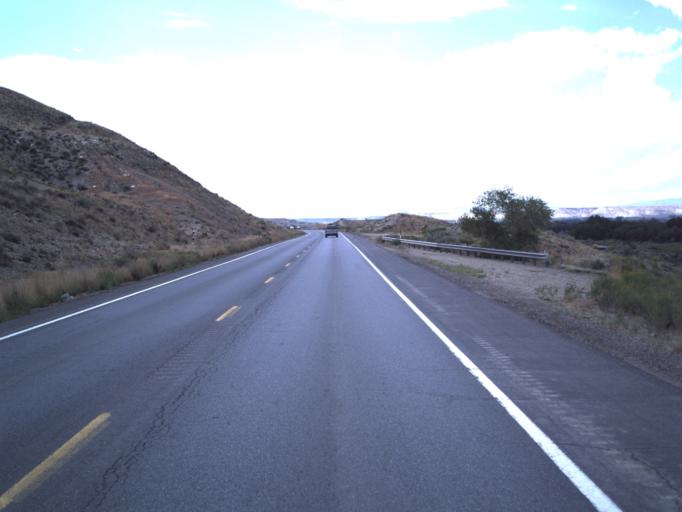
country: US
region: Utah
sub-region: Duchesne County
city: Duchesne
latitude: 40.1564
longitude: -110.2528
